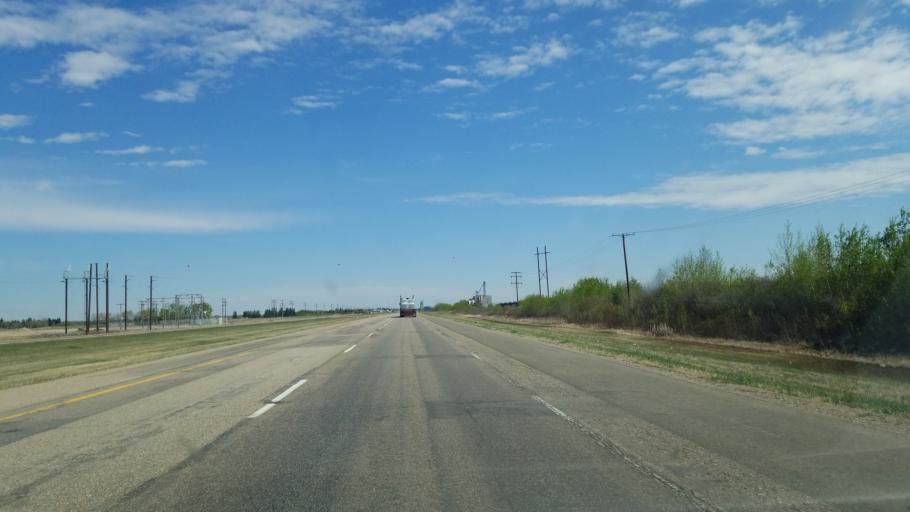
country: CA
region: Saskatchewan
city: Lloydminster
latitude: 53.1397
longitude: -109.6546
